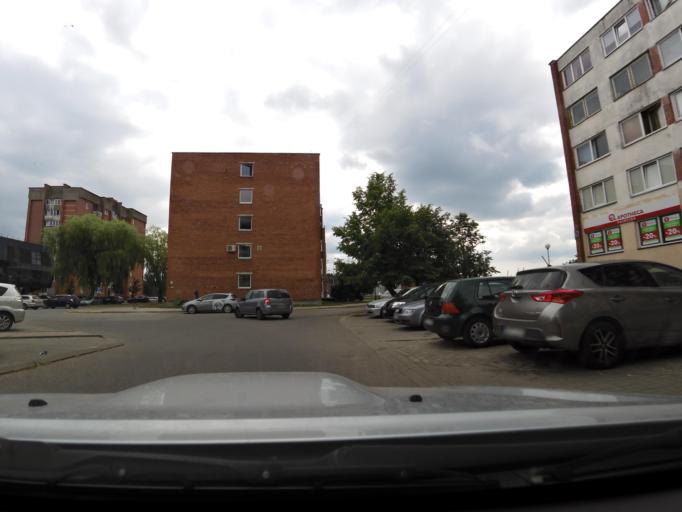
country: LT
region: Klaipedos apskritis
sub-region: Klaipeda
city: Klaipeda
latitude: 55.6946
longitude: 21.1488
